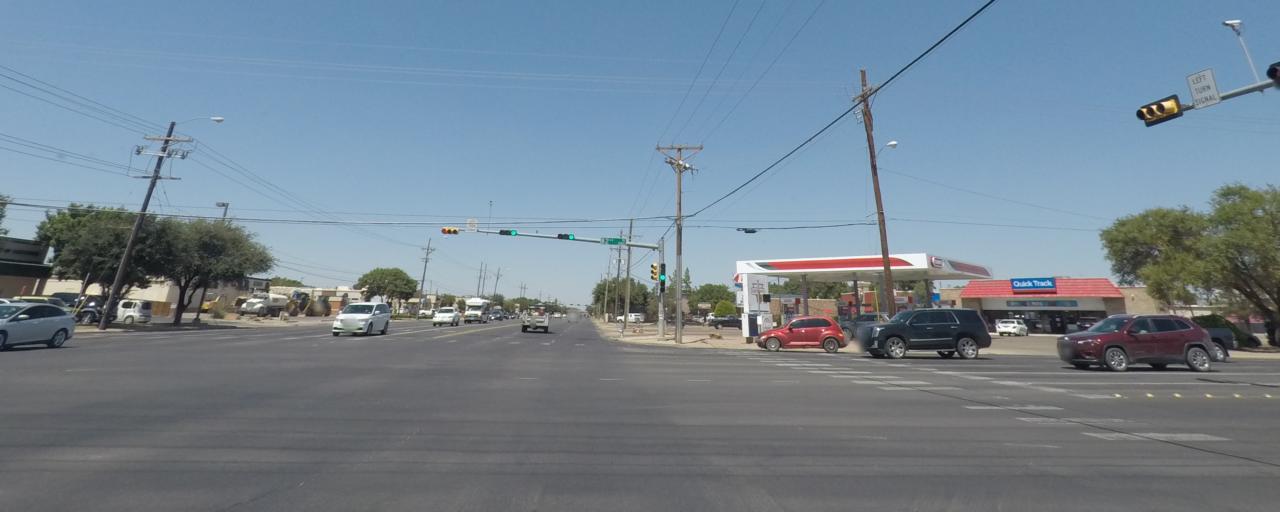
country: US
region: Texas
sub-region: Lubbock County
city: Lubbock
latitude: 33.5196
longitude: -101.8876
